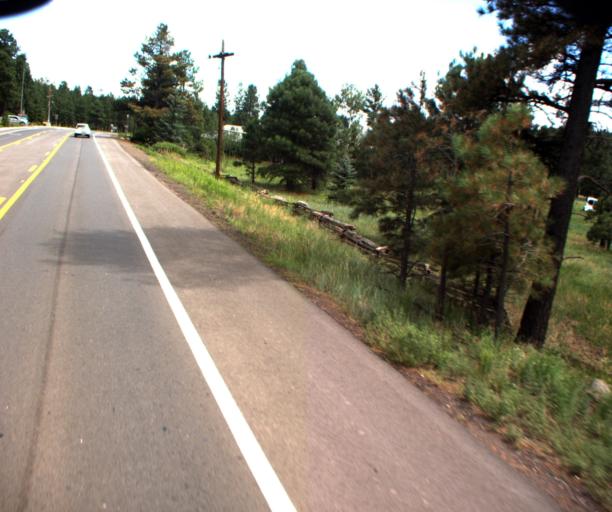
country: US
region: Arizona
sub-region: Coconino County
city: Flagstaff
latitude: 35.2334
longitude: -111.6631
